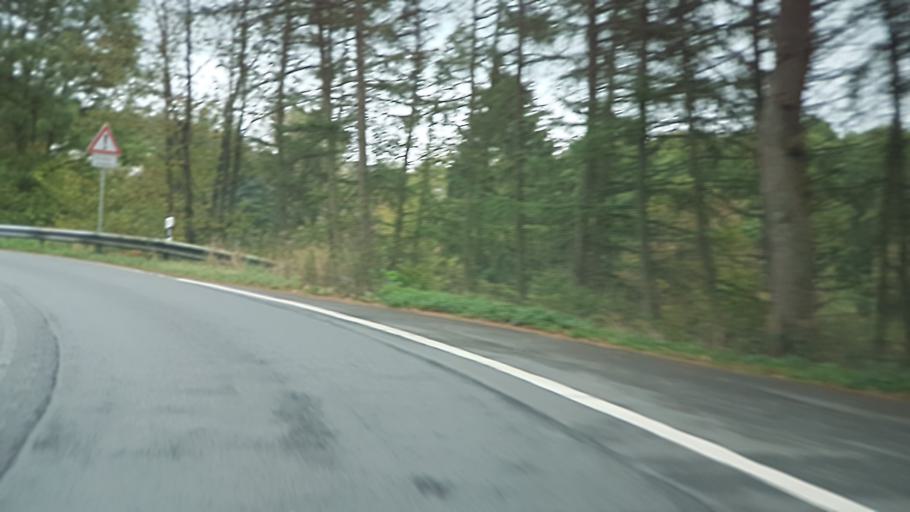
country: DE
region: North Rhine-Westphalia
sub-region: Regierungsbezirk Arnsberg
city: Attendorn
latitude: 51.1467
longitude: 7.8594
